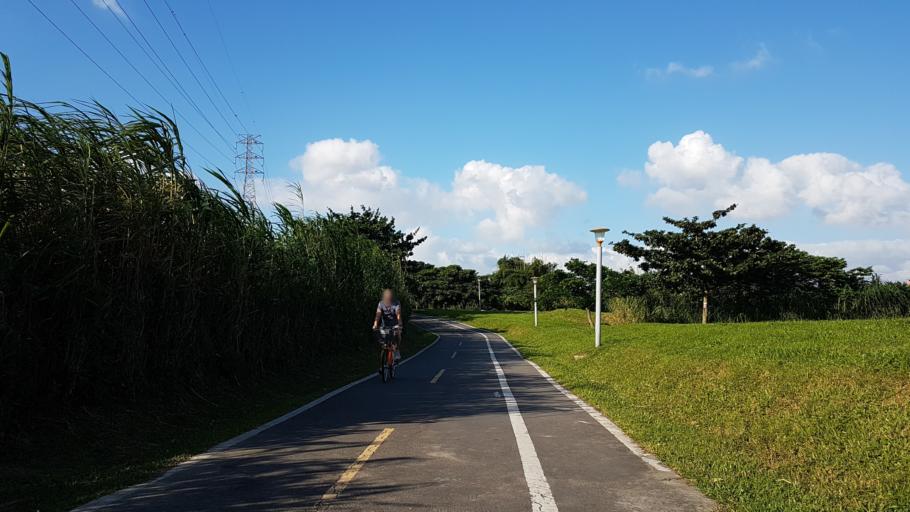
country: TW
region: Taipei
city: Taipei
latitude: 25.0038
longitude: 121.5307
